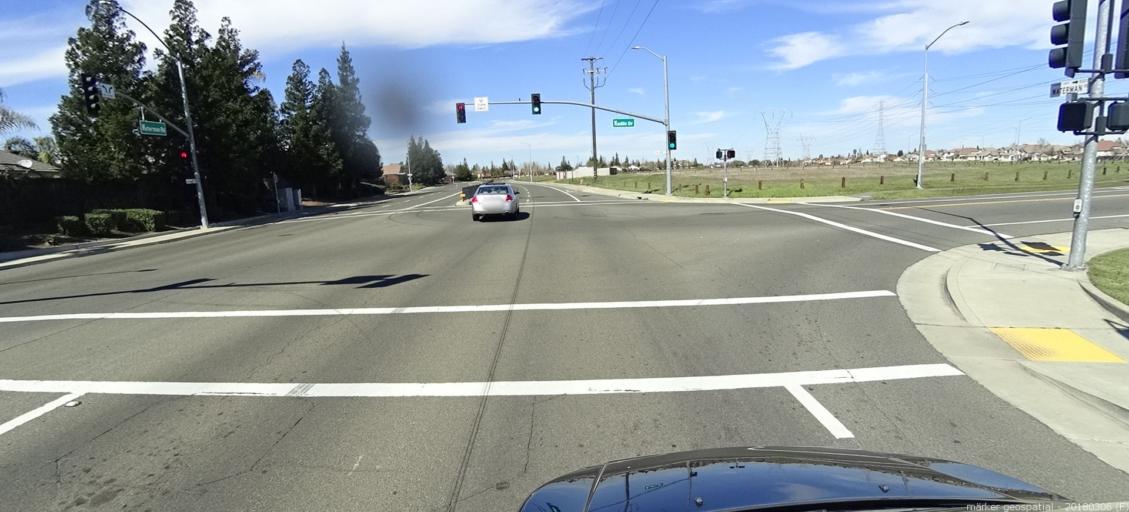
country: US
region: California
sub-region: Sacramento County
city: Vineyard
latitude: 38.4553
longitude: -121.3532
